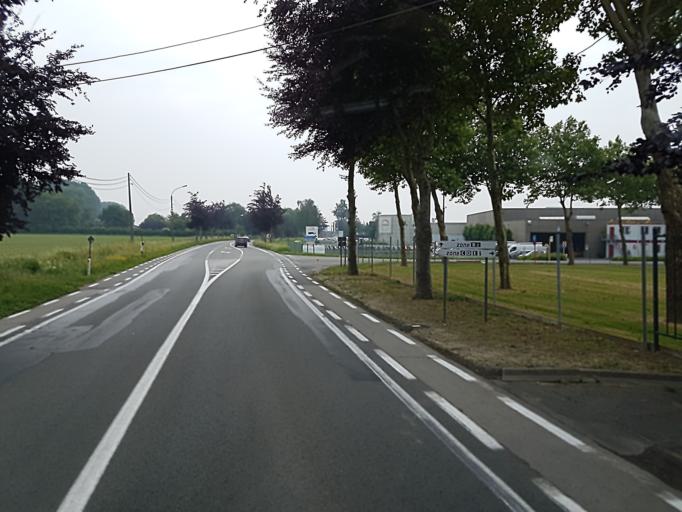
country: BE
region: Flanders
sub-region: Provincie West-Vlaanderen
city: Tielt
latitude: 50.9836
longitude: 3.3417
